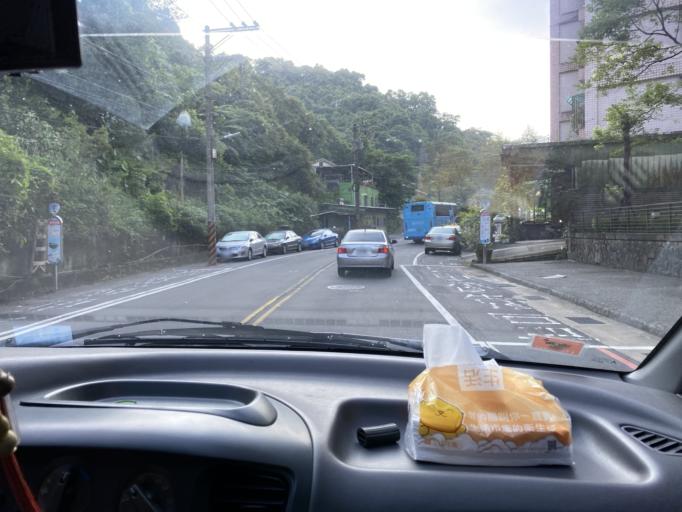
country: TW
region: Taiwan
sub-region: Keelung
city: Keelung
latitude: 25.0985
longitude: 121.7380
